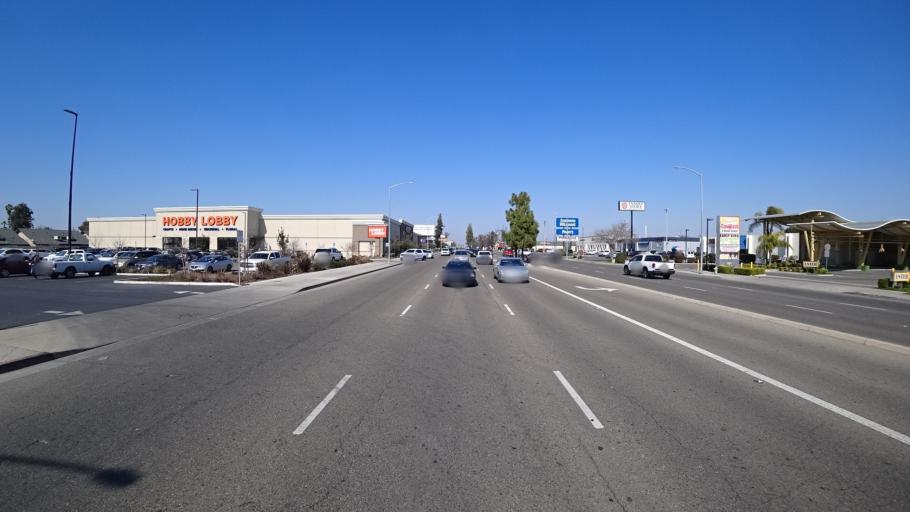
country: US
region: California
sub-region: Fresno County
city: Fresno
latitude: 36.8324
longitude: -119.7904
